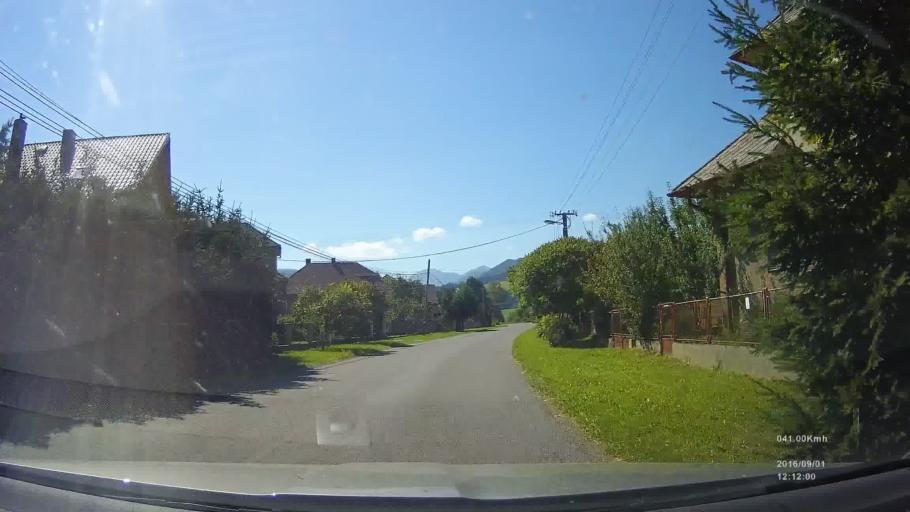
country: SK
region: Zilinsky
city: Ruzomberok
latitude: 49.0600
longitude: 19.4328
